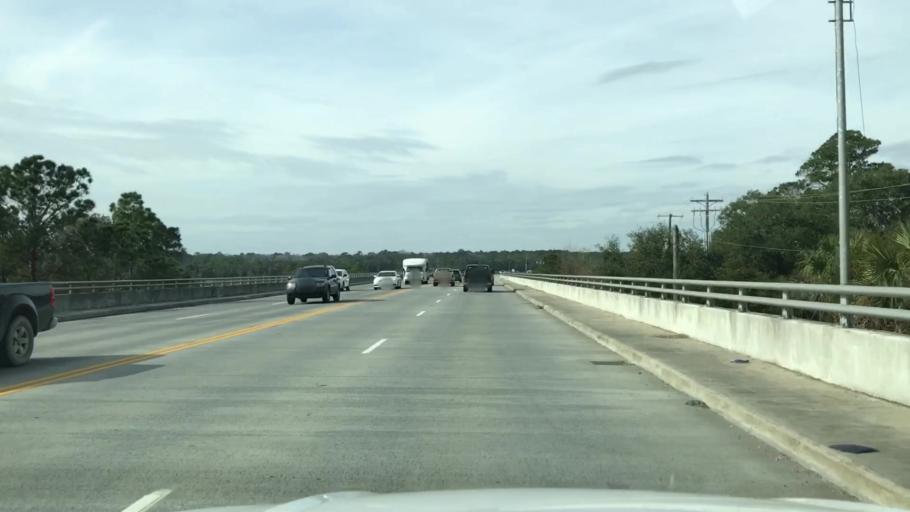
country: US
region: South Carolina
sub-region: Charleston County
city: Charleston
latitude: 32.7519
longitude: -80.0179
